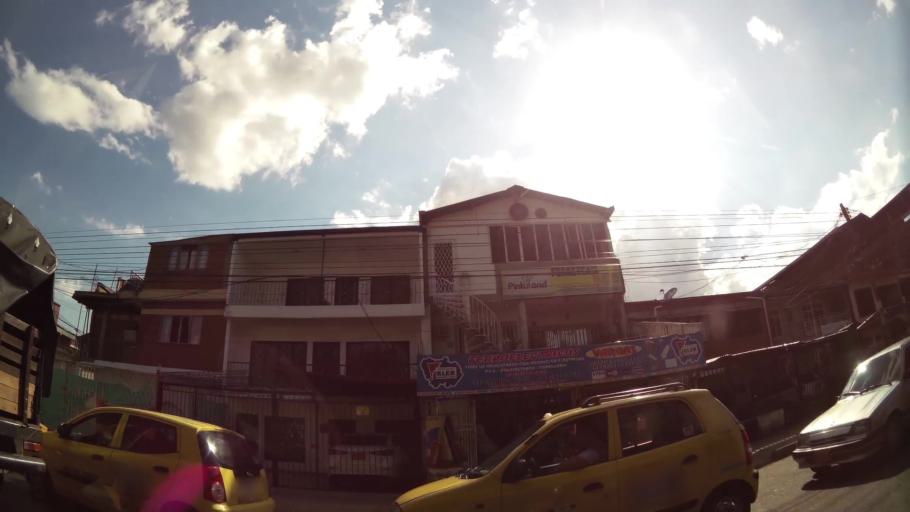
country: CO
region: Valle del Cauca
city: Cali
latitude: 3.4173
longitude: -76.5061
